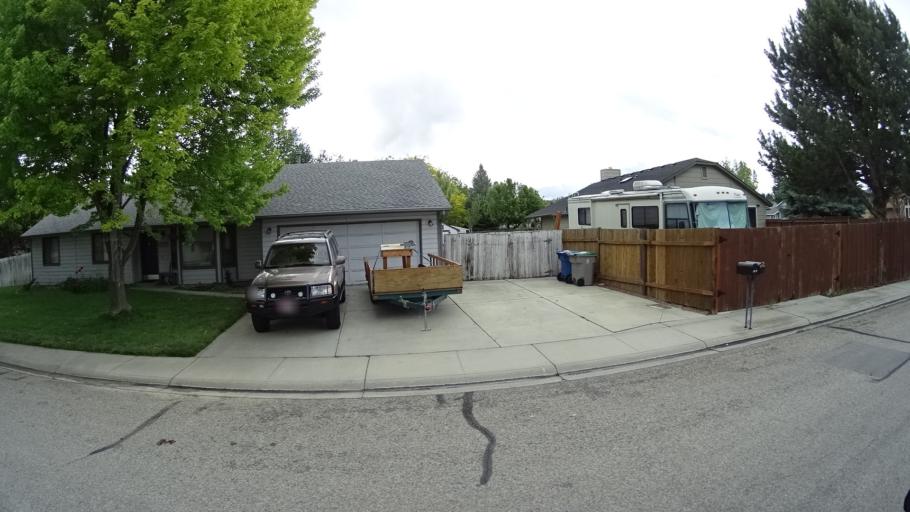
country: US
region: Idaho
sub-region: Ada County
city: Garden City
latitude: 43.6767
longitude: -116.2725
